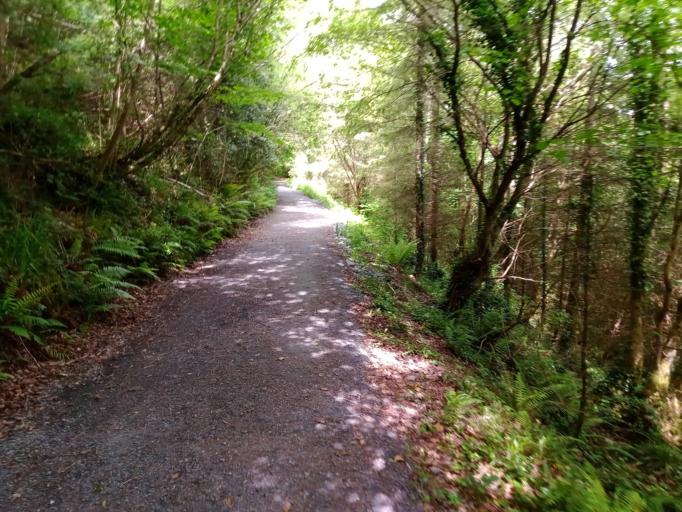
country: IE
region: Leinster
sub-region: Kilkenny
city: Thomastown
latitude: 52.4777
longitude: -7.0475
